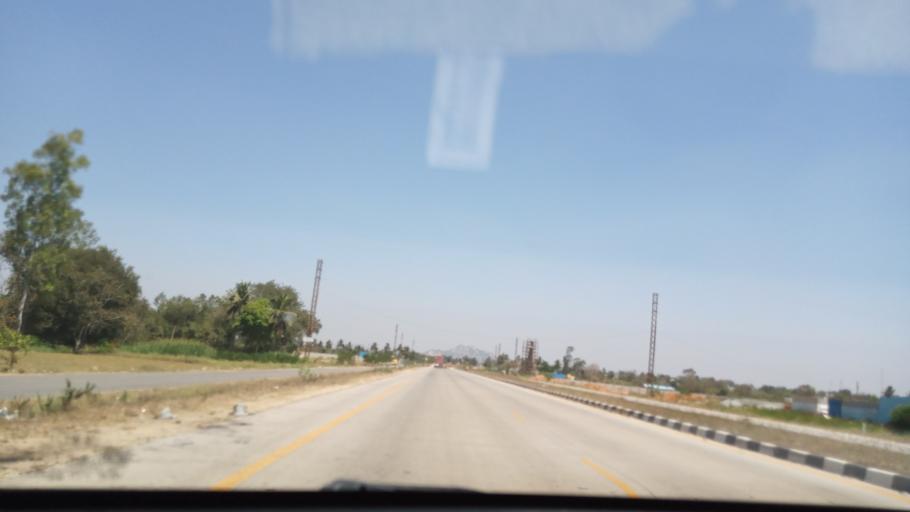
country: IN
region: Andhra Pradesh
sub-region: Chittoor
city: Palmaner
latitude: 13.2069
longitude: 78.7241
